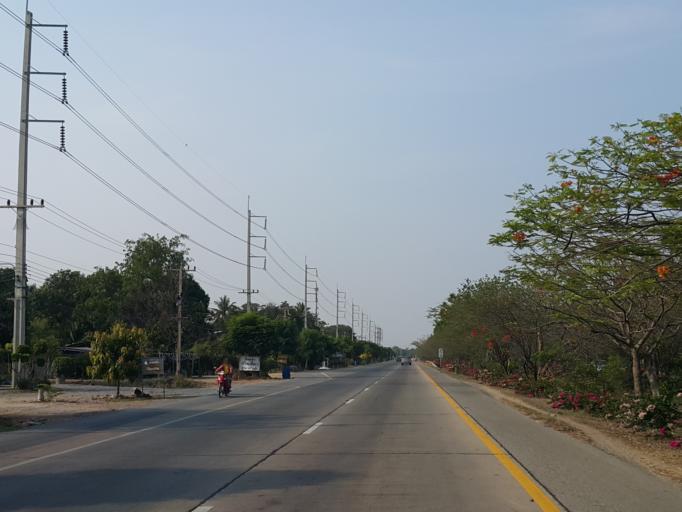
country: TH
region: Suphan Buri
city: Doem Bang Nang Buat
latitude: 14.9141
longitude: 100.0831
